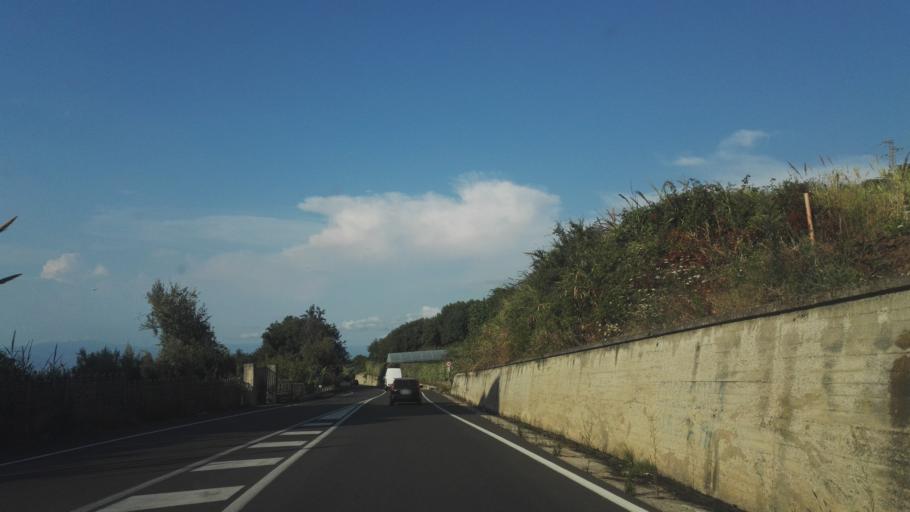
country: IT
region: Calabria
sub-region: Provincia di Vibo-Valentia
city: Sant'Onofrio
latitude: 38.7159
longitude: 16.1439
